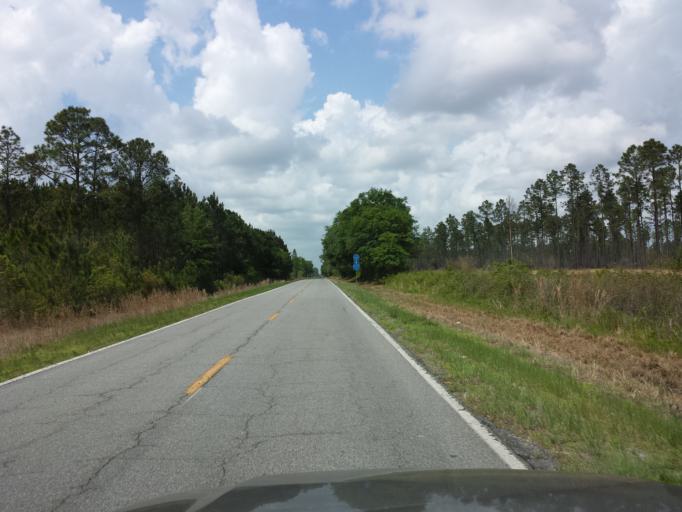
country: US
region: Georgia
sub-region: Echols County
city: Statenville
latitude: 30.6283
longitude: -83.1228
